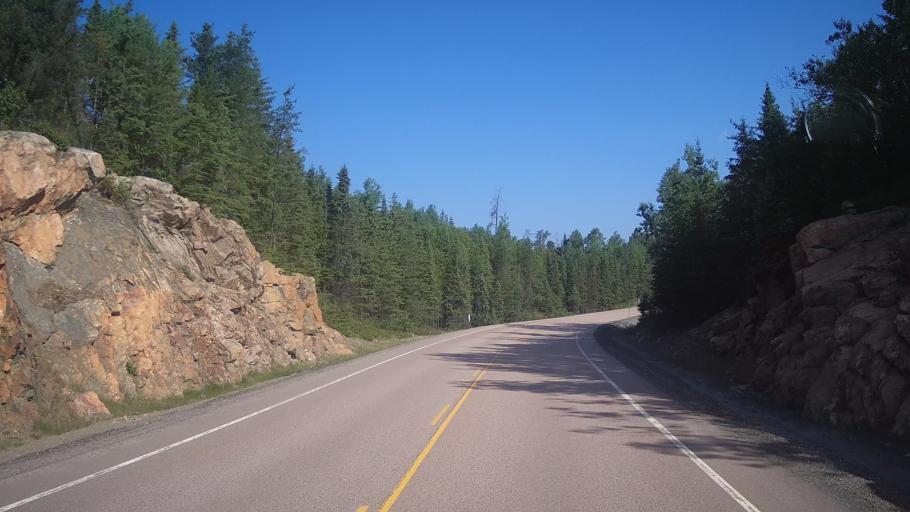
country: CA
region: Ontario
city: Rayside-Balfour
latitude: 46.9805
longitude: -81.6333
